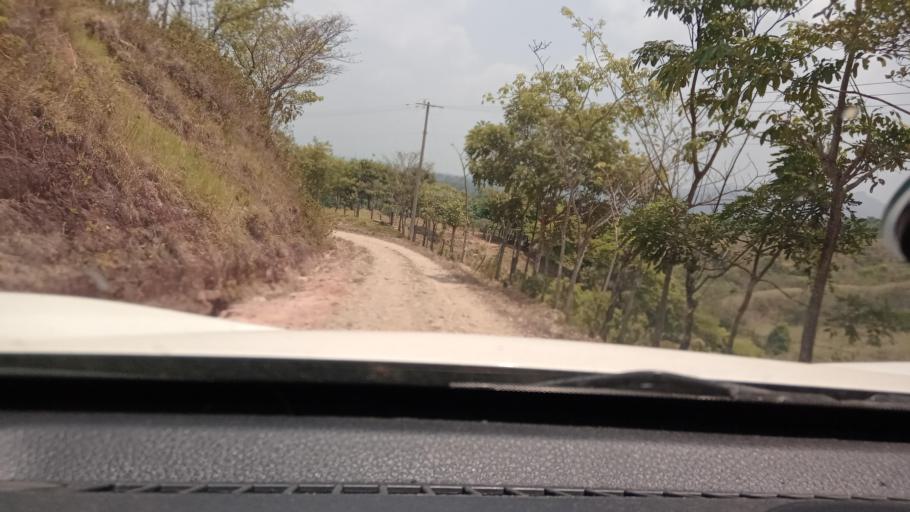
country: MX
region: Tabasco
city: Chontalpa
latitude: 17.5552
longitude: -93.7328
